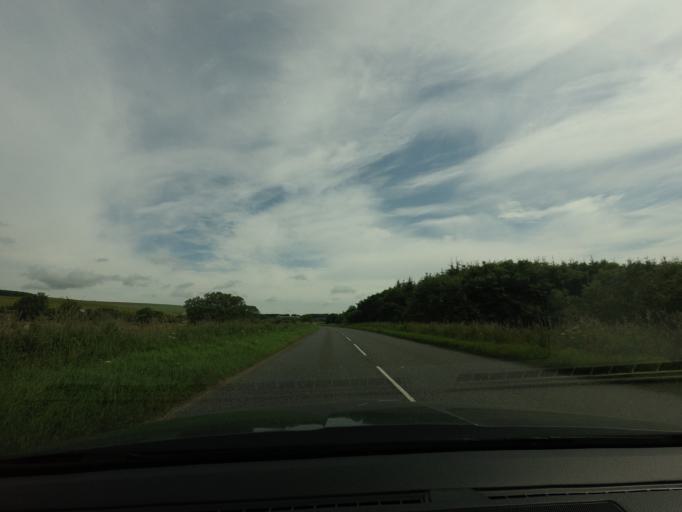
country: GB
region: Scotland
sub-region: Aberdeenshire
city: Turriff
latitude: 57.5997
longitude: -2.2824
